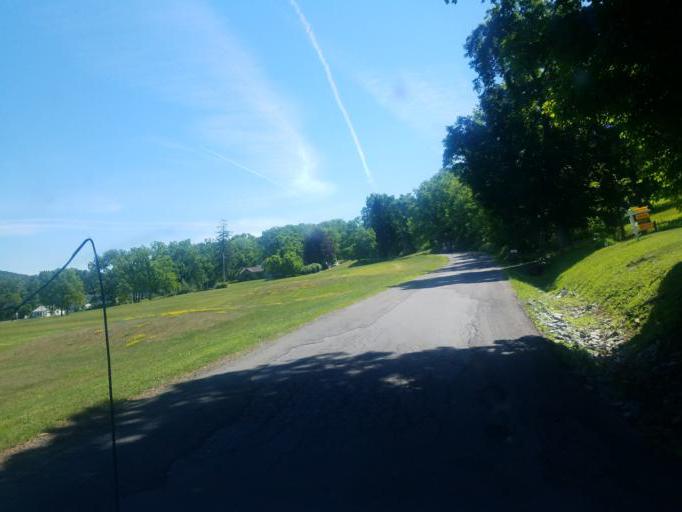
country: US
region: New York
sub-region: Ontario County
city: Naples
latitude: 42.7210
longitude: -77.3263
